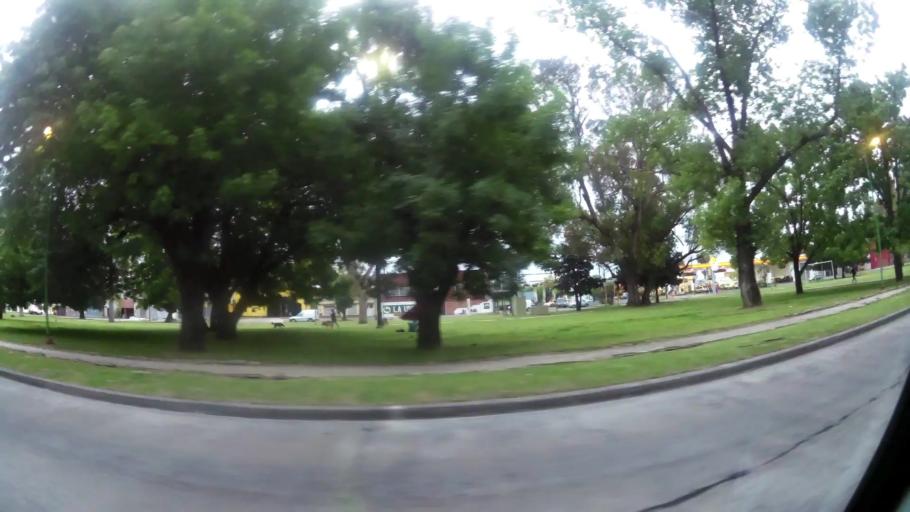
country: AR
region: Buenos Aires
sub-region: Partido de La Plata
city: La Plata
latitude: -34.9101
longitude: -57.9795
